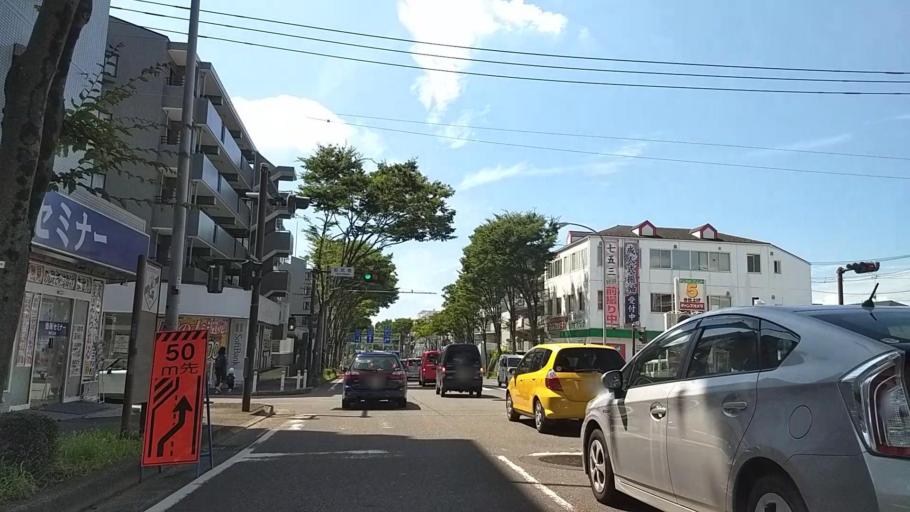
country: JP
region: Tokyo
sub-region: Machida-shi
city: Machida
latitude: 35.5376
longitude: 139.5596
